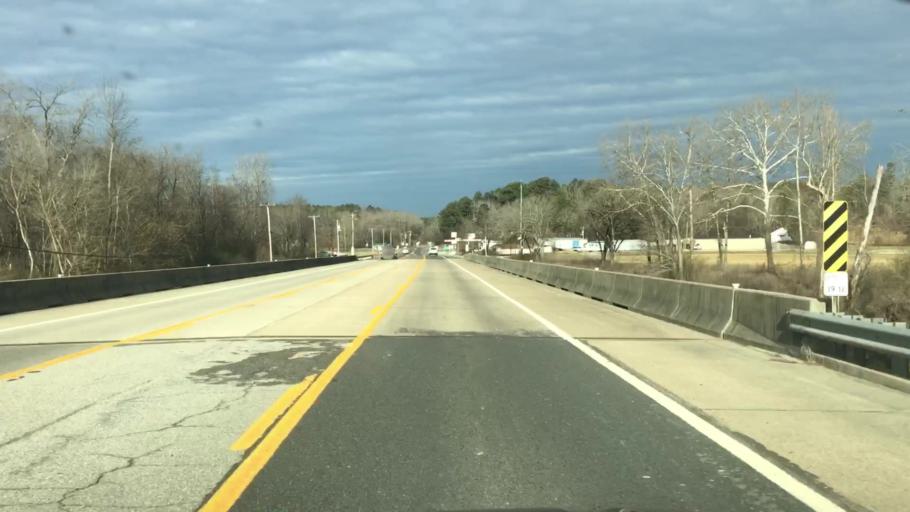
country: US
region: Arkansas
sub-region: Montgomery County
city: Mount Ida
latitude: 34.5601
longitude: -93.6357
